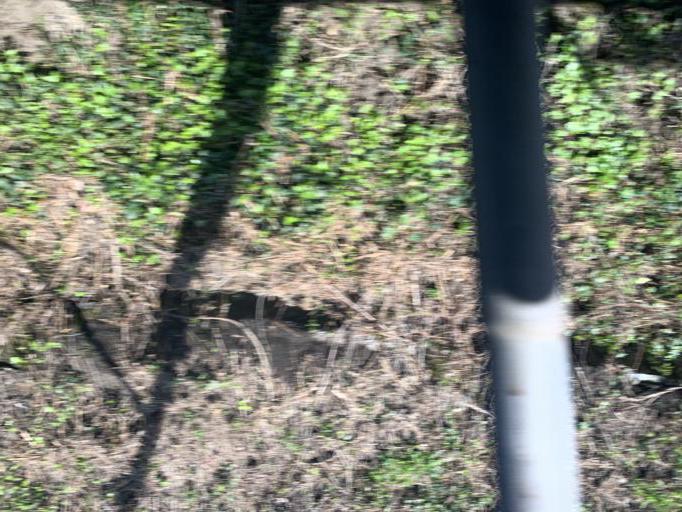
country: IT
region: Latium
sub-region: Citta metropolitana di Roma Capitale
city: Marino
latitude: 41.7806
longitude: 12.6433
